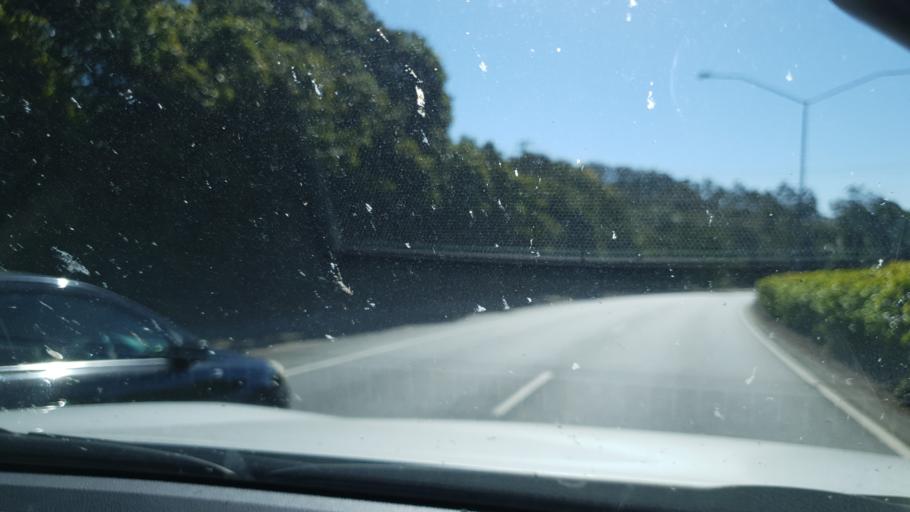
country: AU
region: Queensland
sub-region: Brisbane
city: Bridegman Downs
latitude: -27.3443
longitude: 152.9618
